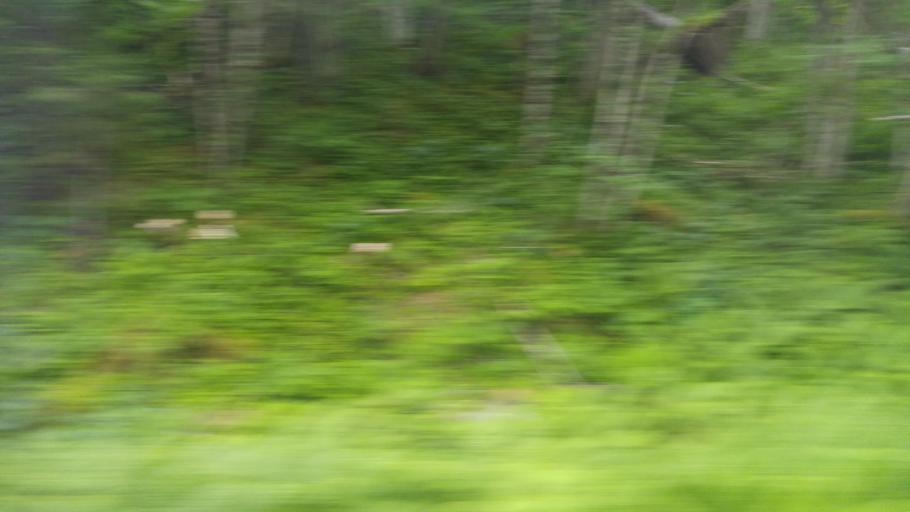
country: NO
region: Nord-Trondelag
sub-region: Meraker
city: Meraker
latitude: 63.4650
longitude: 11.4755
